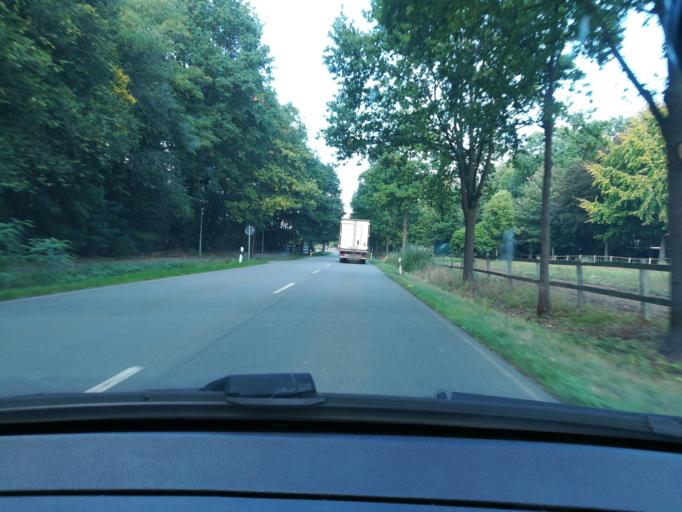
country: DE
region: North Rhine-Westphalia
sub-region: Regierungsbezirk Munster
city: Beelen
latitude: 51.9733
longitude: 8.1437
